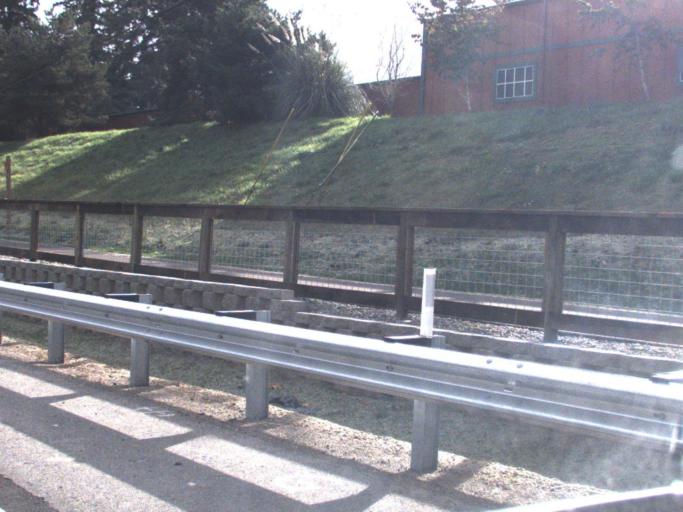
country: US
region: Washington
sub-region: Island County
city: Freeland
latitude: 48.0106
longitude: -122.5383
